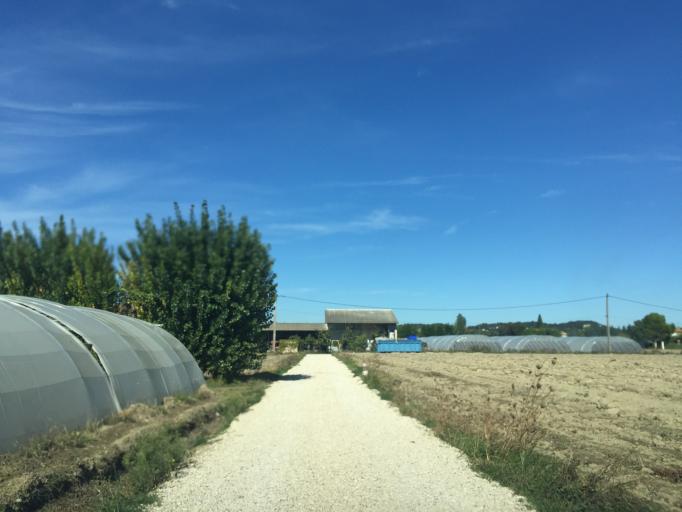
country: FR
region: Provence-Alpes-Cote d'Azur
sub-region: Departement du Vaucluse
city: Piolenc
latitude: 44.1520
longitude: 4.7625
